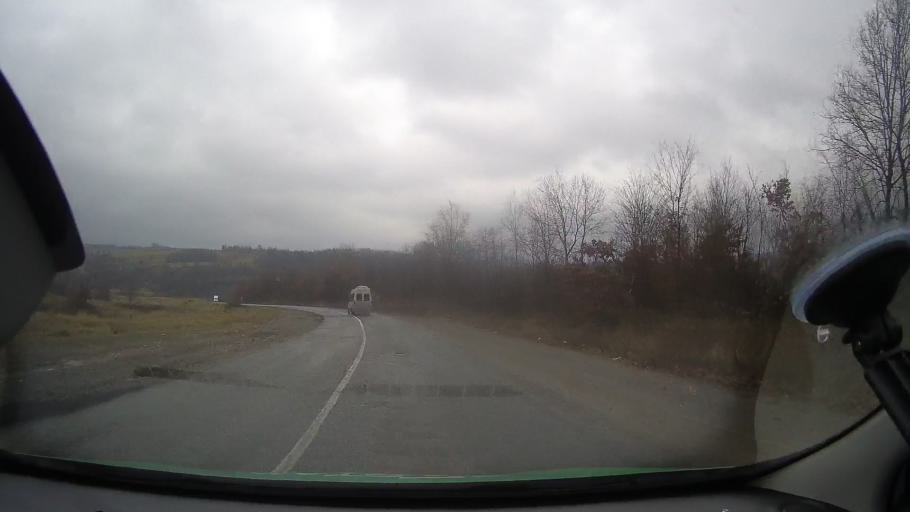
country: RO
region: Arad
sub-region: Comuna Varfurile
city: Varfurile
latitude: 46.2918
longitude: 22.5423
